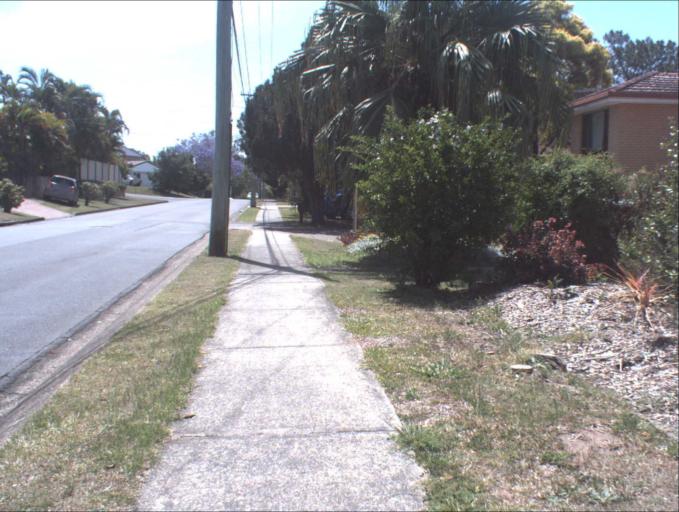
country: AU
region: Queensland
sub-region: Logan
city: Rochedale South
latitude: -27.5960
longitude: 153.1452
